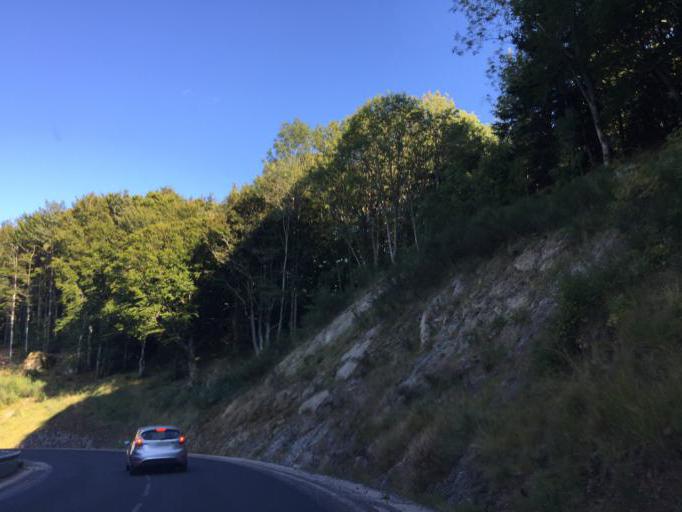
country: FR
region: Auvergne
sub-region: Departement de la Haute-Loire
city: Saugues
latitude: 44.9812
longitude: 3.6219
